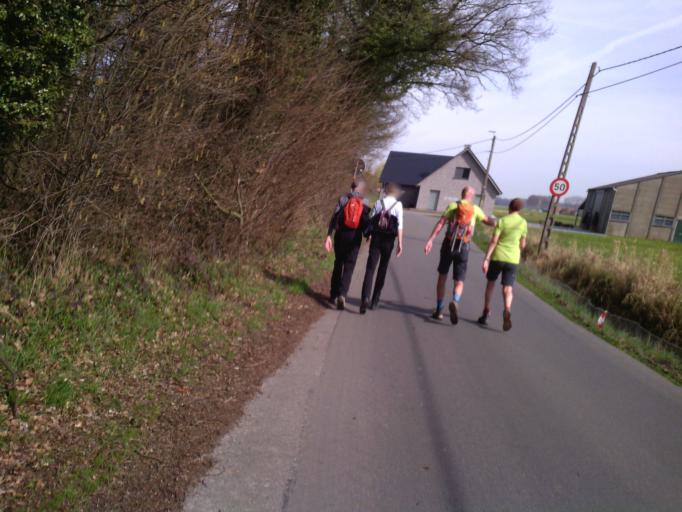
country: BE
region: Flanders
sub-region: Provincie West-Vlaanderen
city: Poperinge
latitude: 50.8690
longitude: 2.7887
